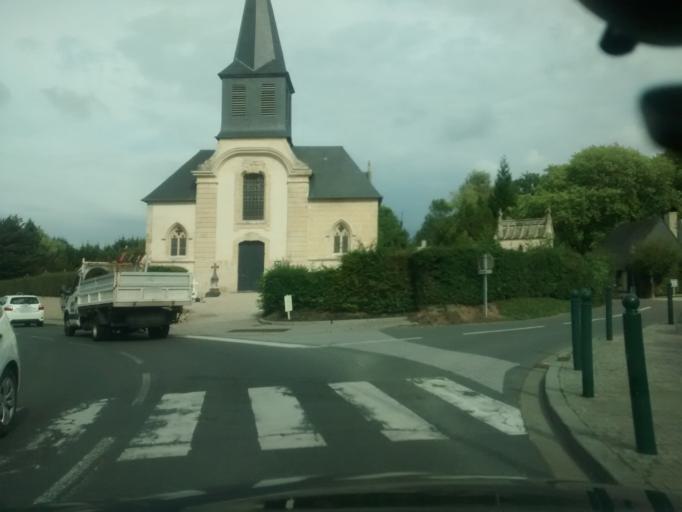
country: FR
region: Lower Normandy
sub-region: Departement du Calvados
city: Deauville
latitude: 49.3232
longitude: 0.0647
